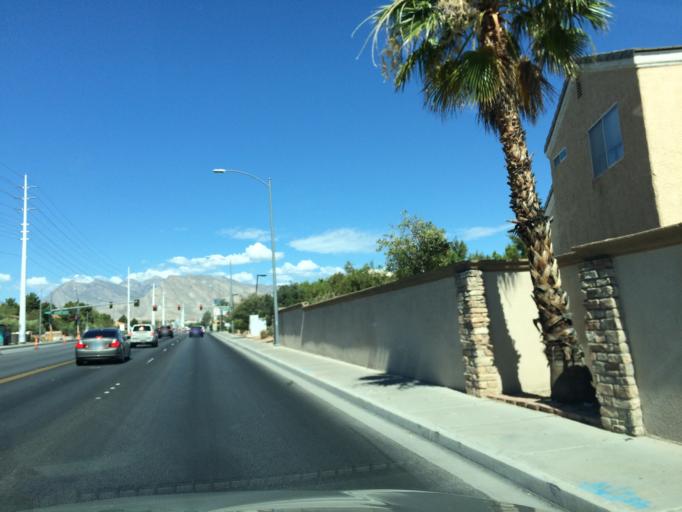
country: US
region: Nevada
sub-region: Clark County
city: Spring Valley
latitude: 36.2187
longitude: -115.2724
